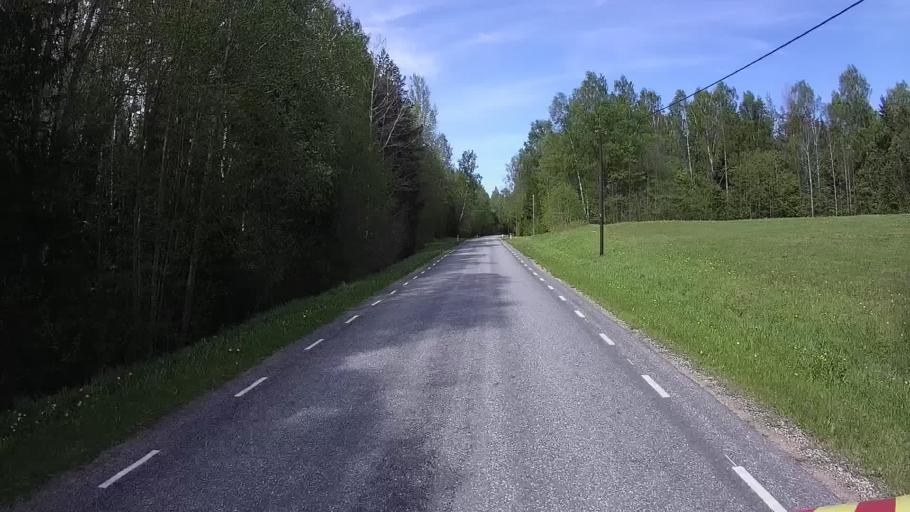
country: EE
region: Valgamaa
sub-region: Valga linn
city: Valga
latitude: 57.6659
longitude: 26.2867
